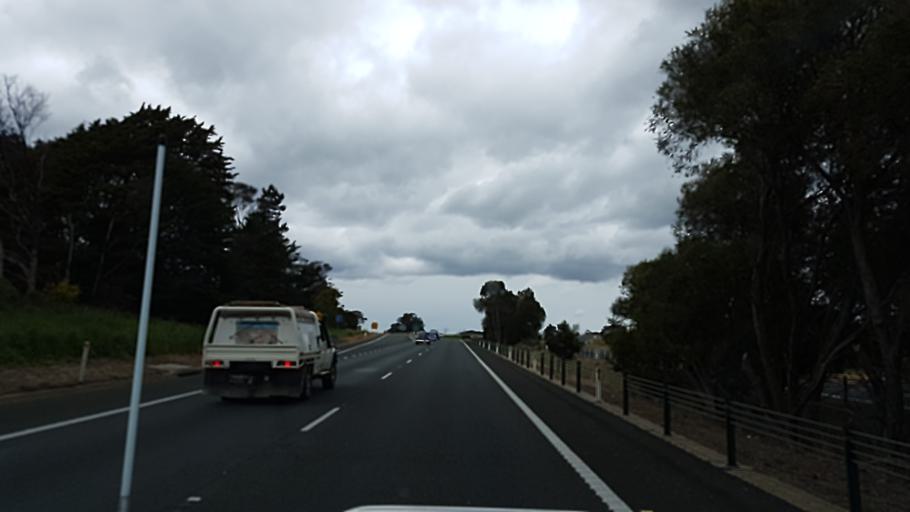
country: AU
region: Victoria
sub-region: Moorabool
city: Bacchus Marsh
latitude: -37.6095
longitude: 144.3131
